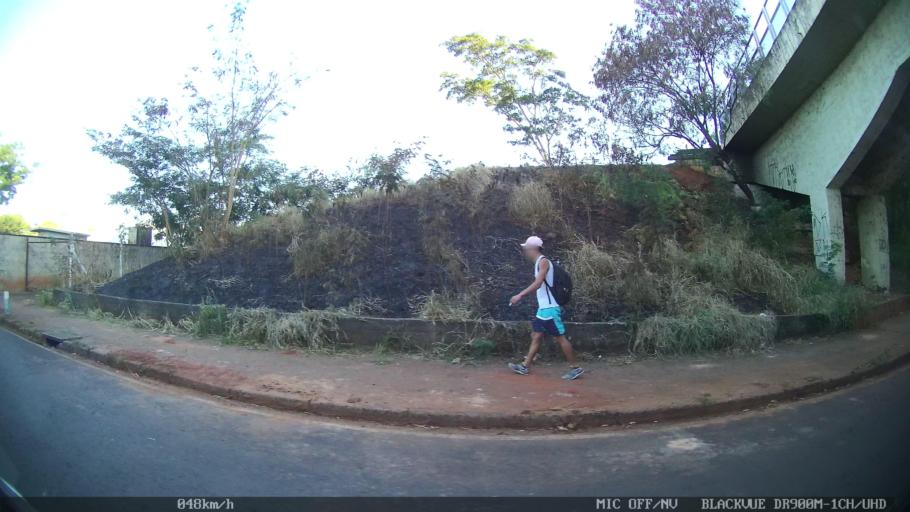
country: BR
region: Sao Paulo
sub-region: Sao Jose Do Rio Preto
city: Sao Jose do Rio Preto
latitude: -20.7968
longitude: -49.3783
